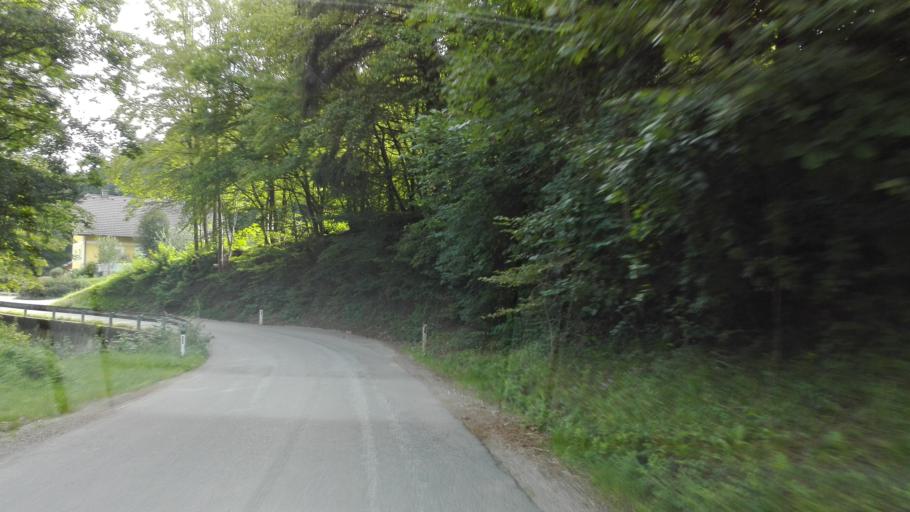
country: AT
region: Lower Austria
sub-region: Politischer Bezirk Sankt Polten
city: Stossing
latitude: 48.1161
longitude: 15.8131
